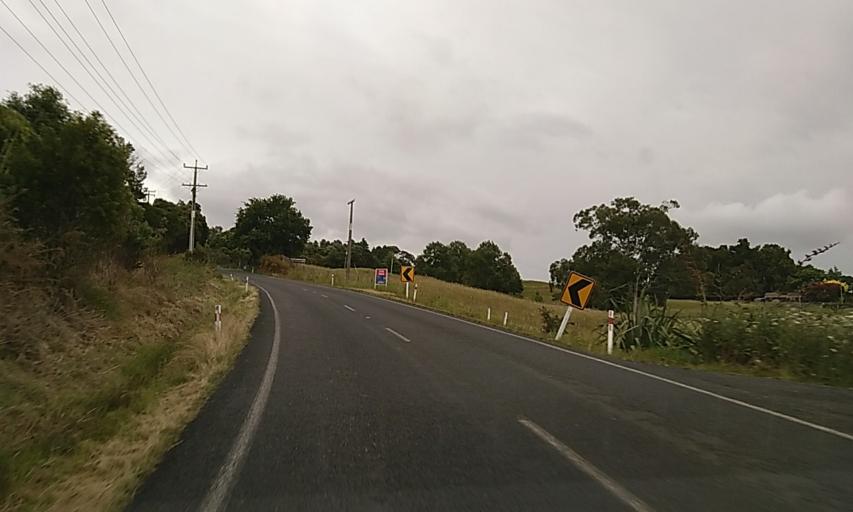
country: NZ
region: Auckland
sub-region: Auckland
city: Pukekohe East
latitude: -37.2984
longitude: 174.9388
